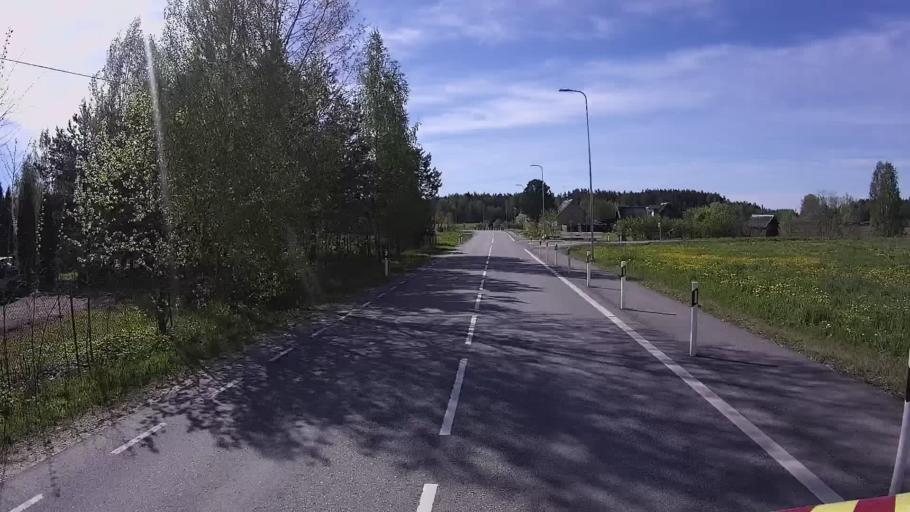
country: EE
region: Polvamaa
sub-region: Raepina vald
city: Rapina
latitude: 58.0008
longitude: 27.5440
